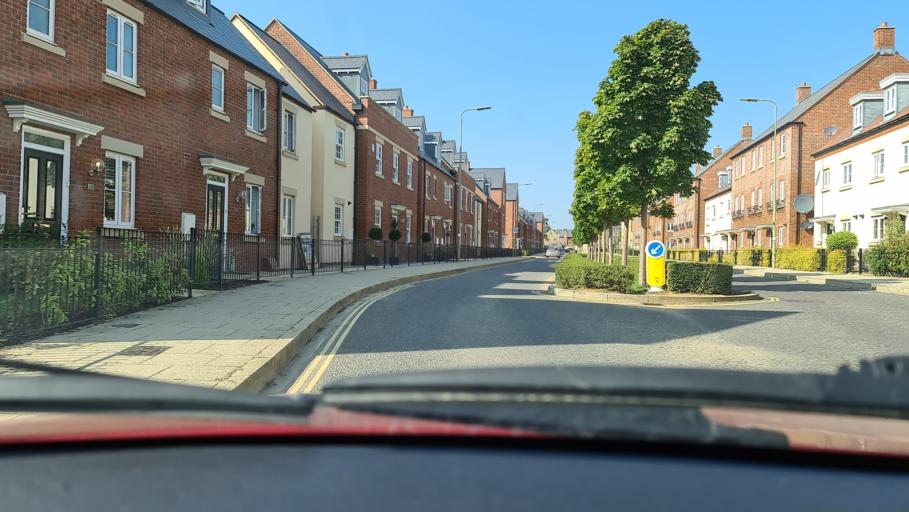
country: GB
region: England
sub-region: Oxfordshire
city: Bicester
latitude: 51.8953
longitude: -1.1724
